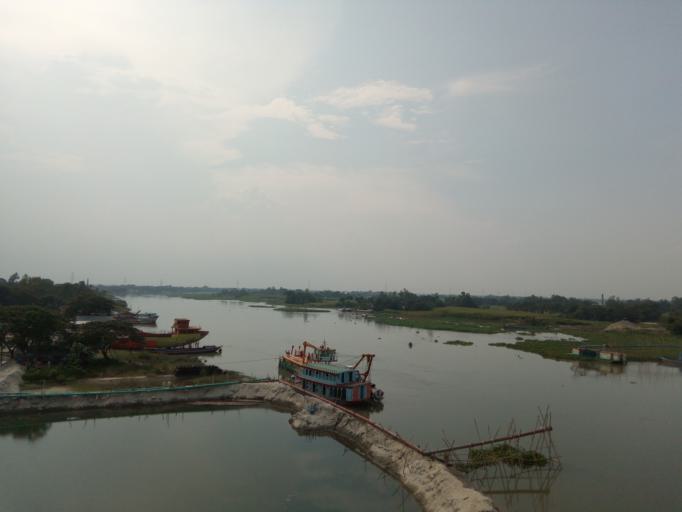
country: BD
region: Dhaka
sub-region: Dhaka
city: Dhaka
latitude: 23.6363
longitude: 90.3460
